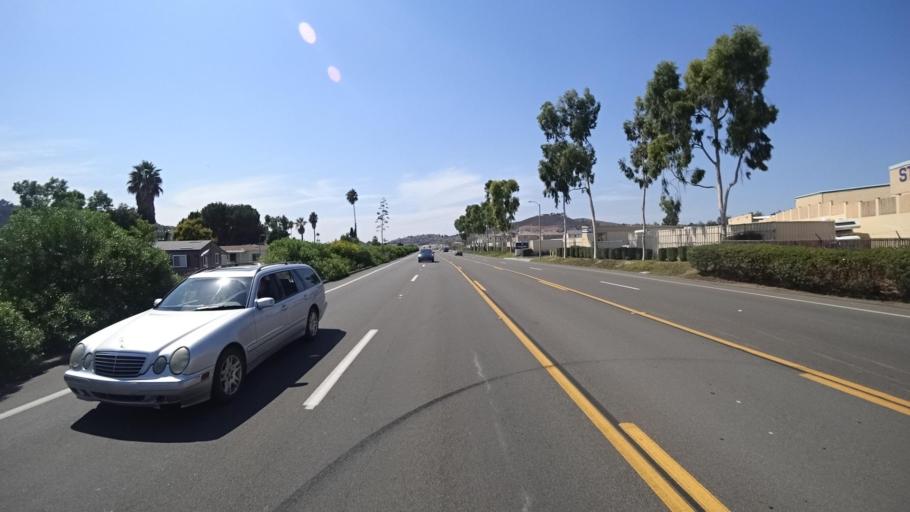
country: US
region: California
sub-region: San Diego County
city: Rancho San Diego
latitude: 32.7292
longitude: -116.9627
